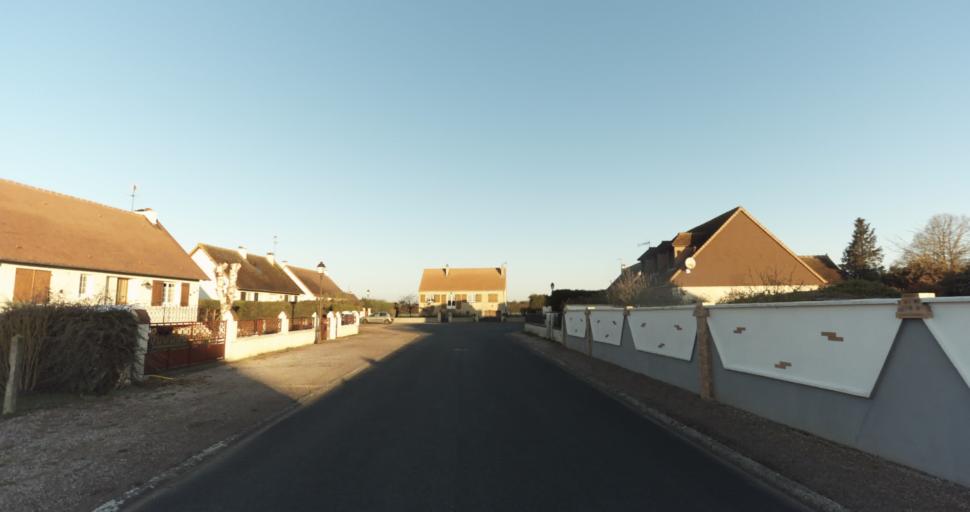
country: FR
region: Lower Normandy
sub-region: Departement du Calvados
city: Saint-Pierre-sur-Dives
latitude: 49.0336
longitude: -0.0286
